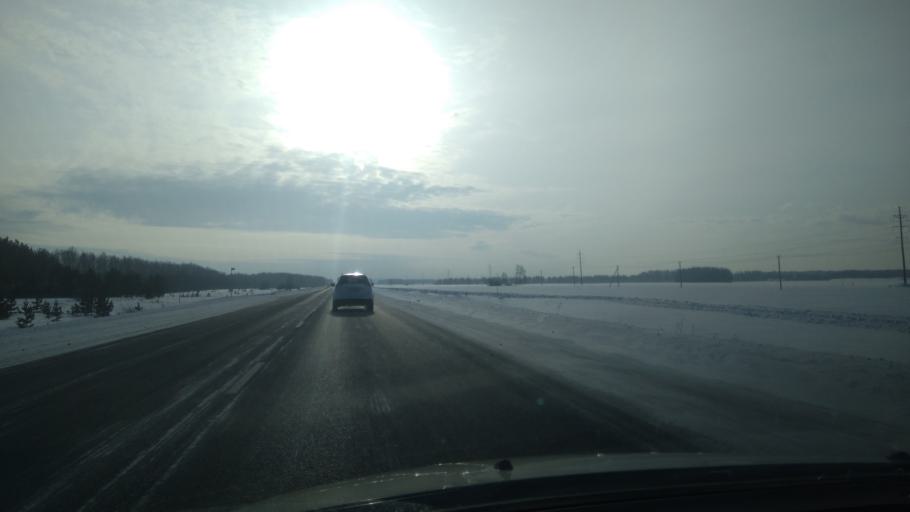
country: RU
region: Sverdlovsk
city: Sukhoy Log
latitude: 56.8535
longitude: 62.0489
